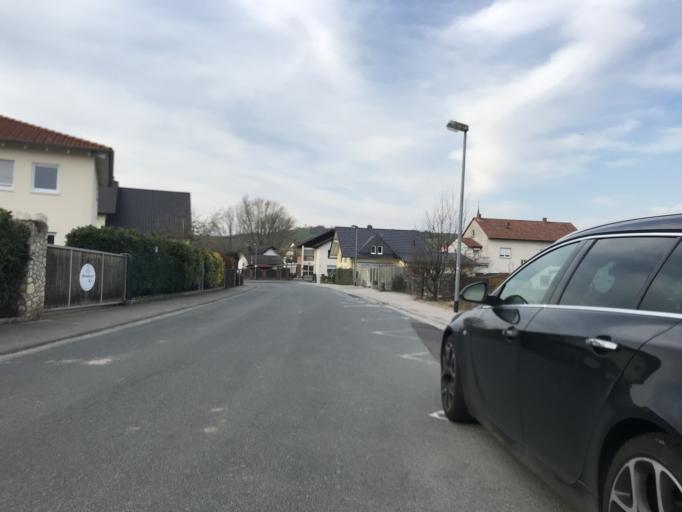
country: DE
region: Rheinland-Pfalz
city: Stadecken-Elsheim
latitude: 49.9096
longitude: 8.1335
